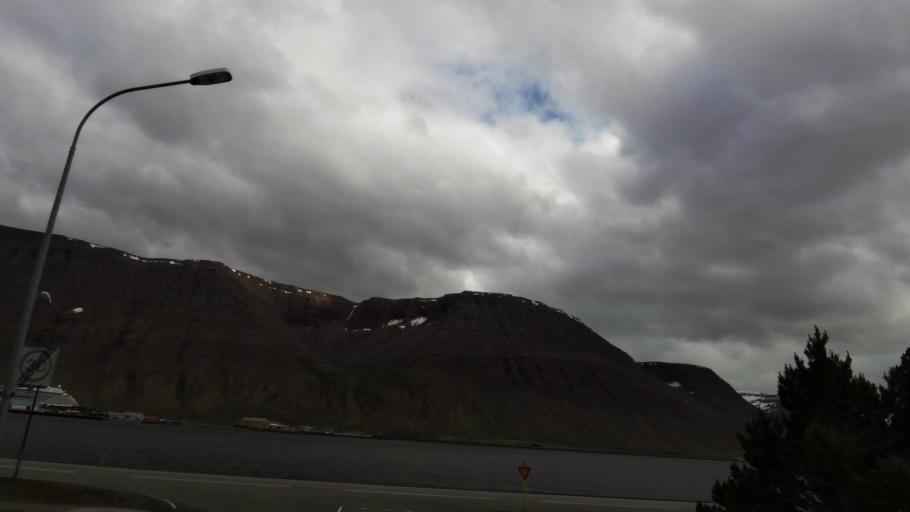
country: IS
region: Westfjords
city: Isafjoerdur
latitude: 66.0714
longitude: -23.1404
